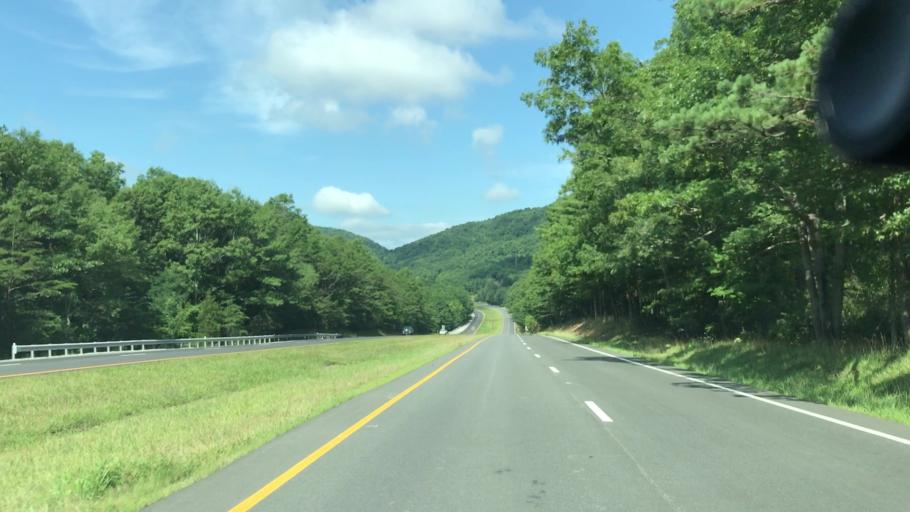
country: US
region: Virginia
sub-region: Montgomery County
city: Blacksburg
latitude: 37.2853
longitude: -80.4570
